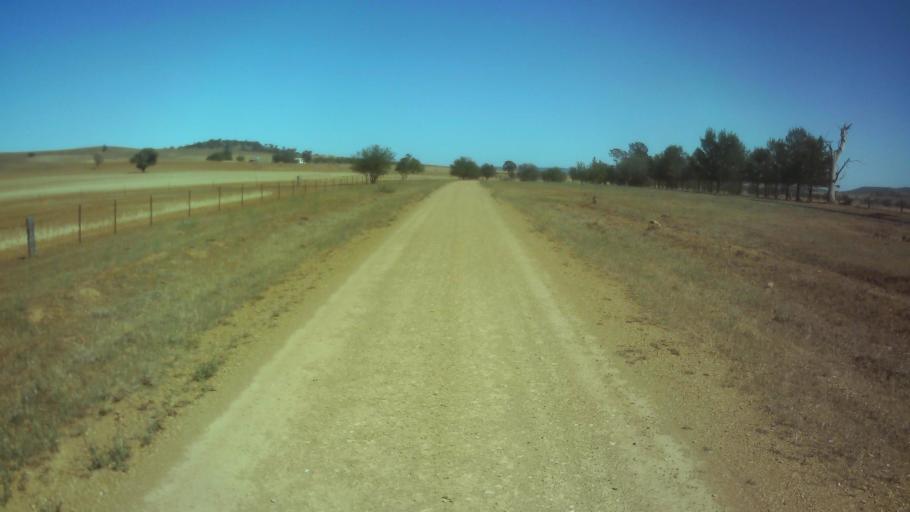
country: AU
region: New South Wales
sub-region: Weddin
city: Grenfell
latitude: -33.9632
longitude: 148.3071
